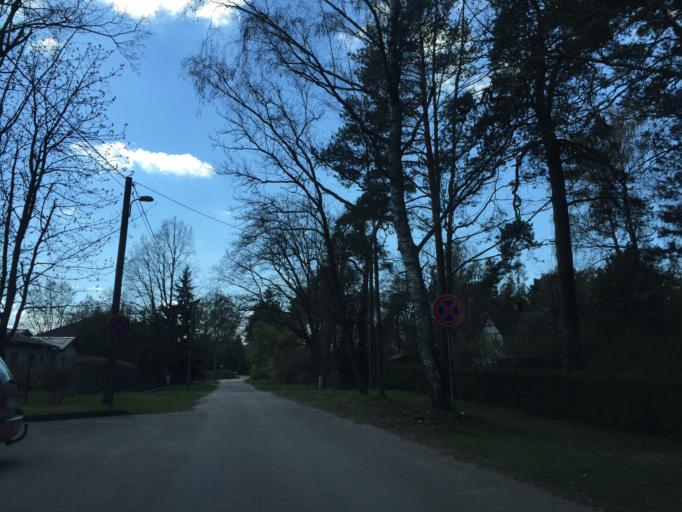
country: LV
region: Saulkrastu
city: Saulkrasti
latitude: 57.2332
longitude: 24.3931
